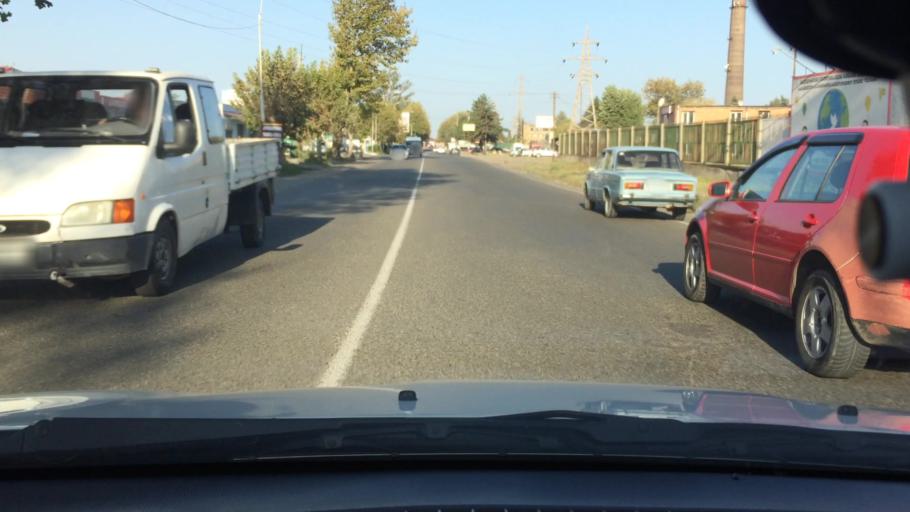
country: GE
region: Imereti
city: Zestap'oni
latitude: 42.1169
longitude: 43.0205
